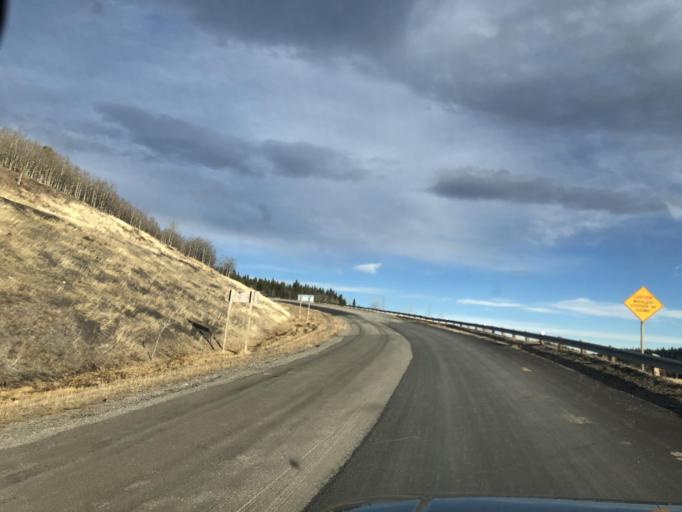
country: CA
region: Alberta
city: Cochrane
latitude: 51.0387
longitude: -114.8702
